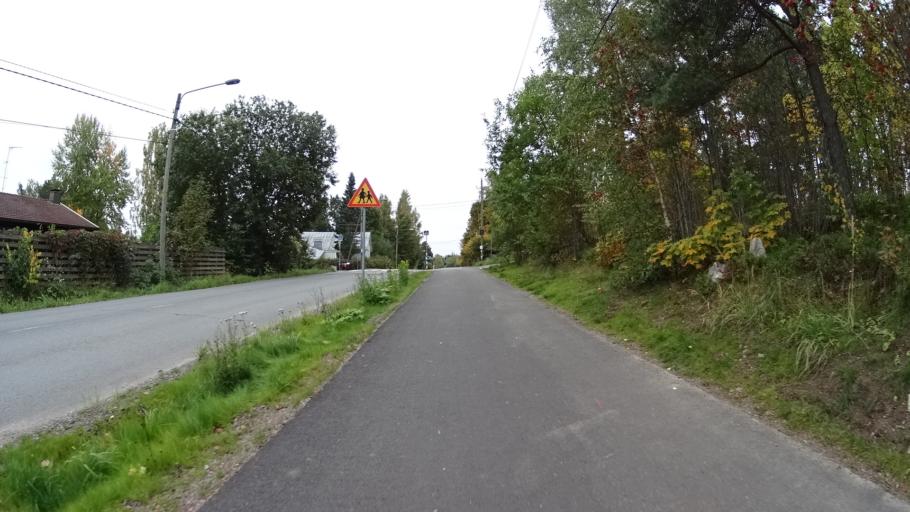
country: FI
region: Uusimaa
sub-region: Helsinki
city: Kilo
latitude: 60.2391
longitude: 24.8086
